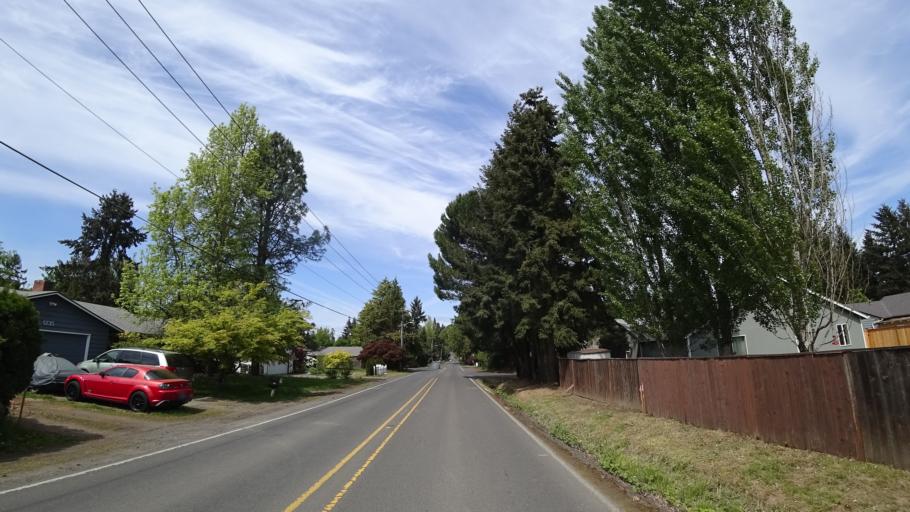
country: US
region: Oregon
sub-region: Washington County
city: Aloha
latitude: 45.4781
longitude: -122.8816
